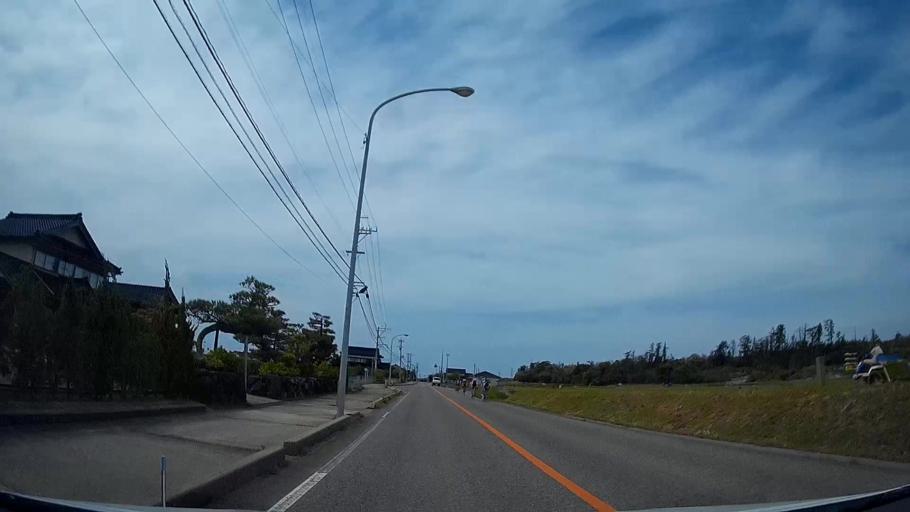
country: JP
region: Ishikawa
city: Hakui
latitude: 37.0350
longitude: 136.7464
